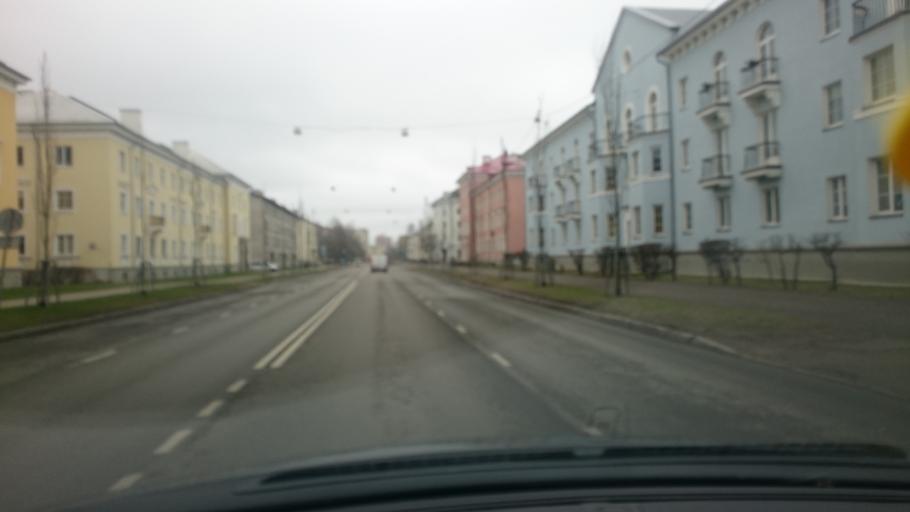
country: EE
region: Harju
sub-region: Tallinna linn
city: Tallinn
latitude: 59.4533
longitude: 24.6920
